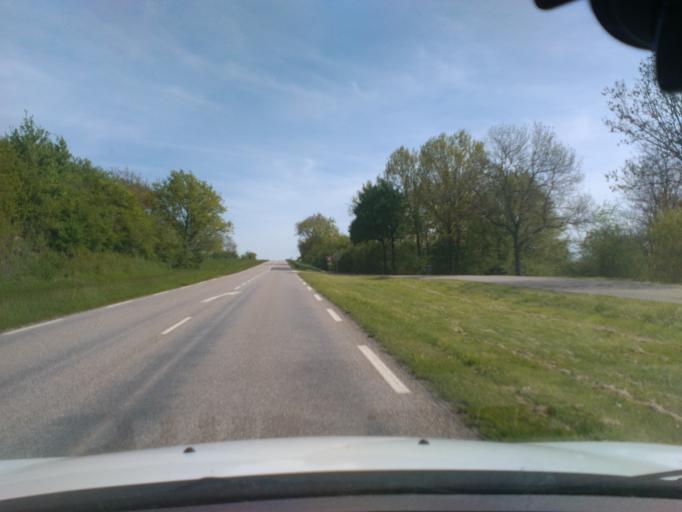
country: FR
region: Lorraine
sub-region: Departement des Vosges
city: Mirecourt
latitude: 48.3302
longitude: 6.1345
